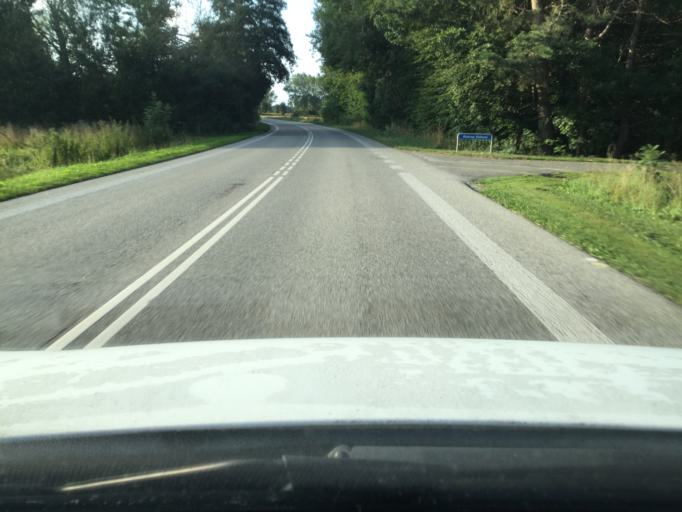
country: DK
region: Zealand
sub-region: Lolland Kommune
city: Rodby
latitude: 54.7700
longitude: 11.2999
